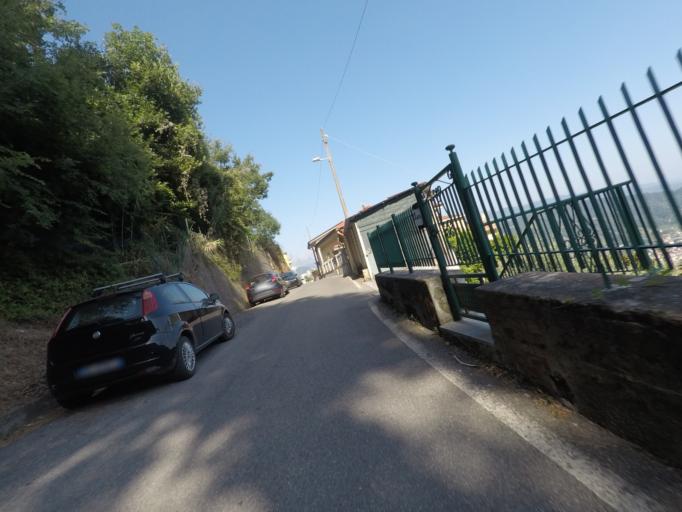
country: IT
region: Tuscany
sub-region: Provincia di Massa-Carrara
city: Carrara
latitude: 44.0754
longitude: 10.0649
